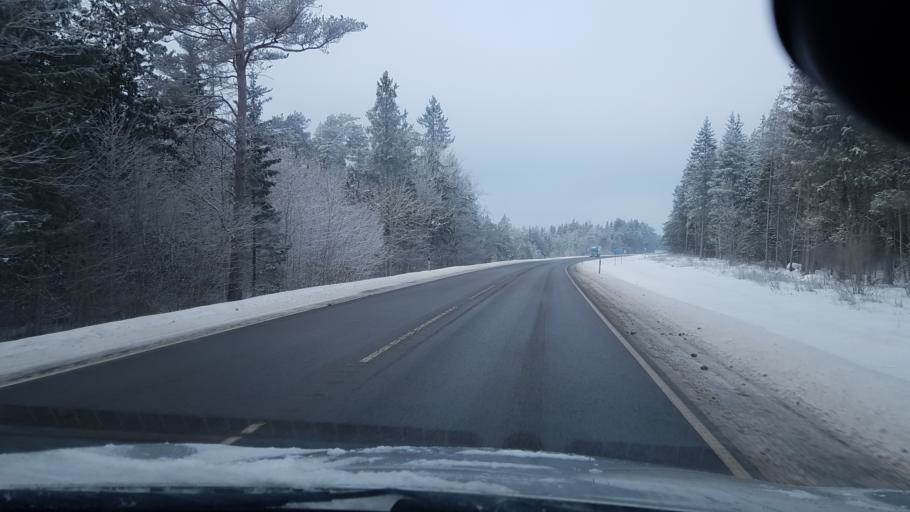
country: EE
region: Harju
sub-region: Keila linn
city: Keila
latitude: 59.3307
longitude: 24.2958
